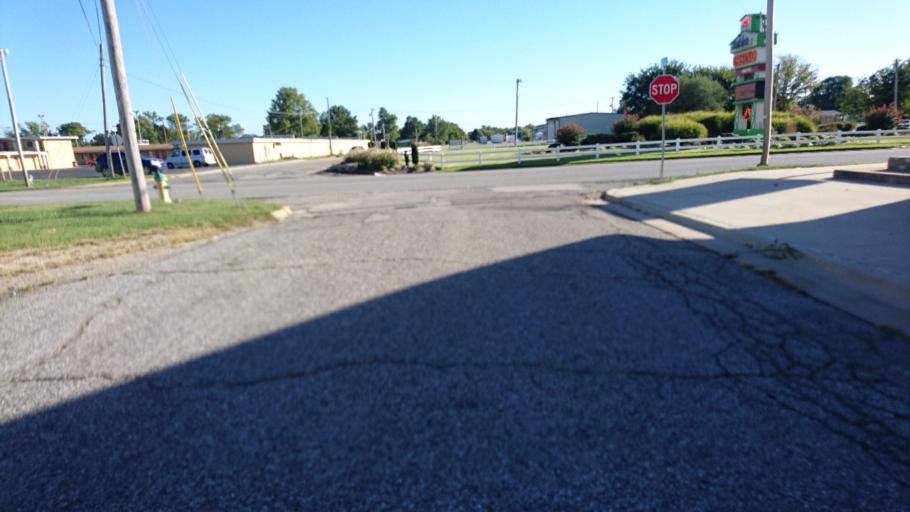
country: US
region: Oklahoma
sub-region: Ottawa County
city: Miami
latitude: 36.8713
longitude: -94.8691
